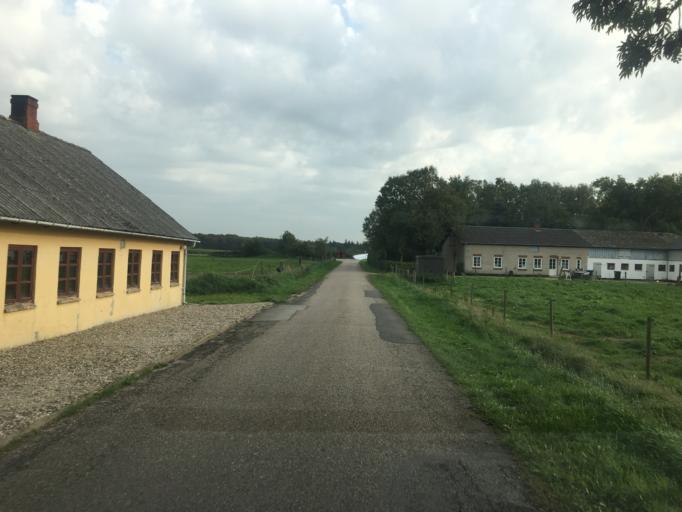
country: DK
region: South Denmark
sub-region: Tonder Kommune
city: Logumkloster
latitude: 54.9828
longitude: 9.0098
